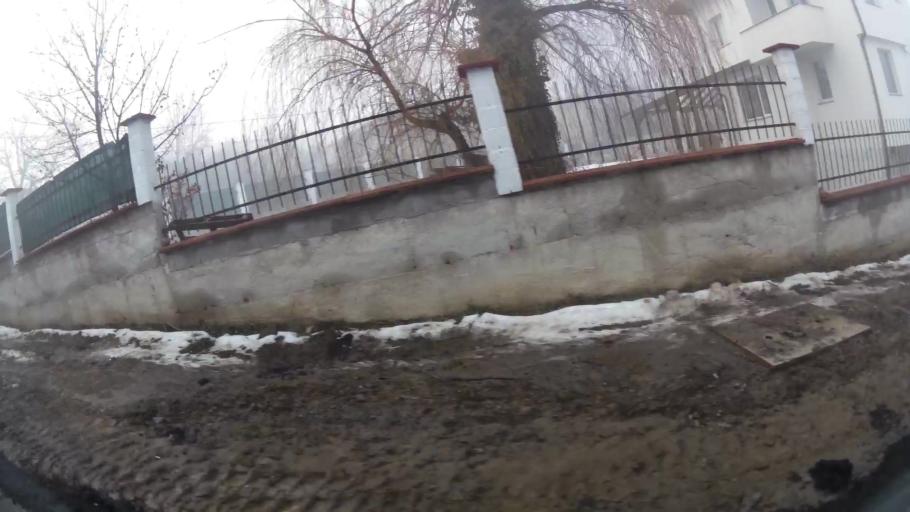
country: BG
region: Sofia-Capital
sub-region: Stolichna Obshtina
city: Sofia
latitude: 42.6554
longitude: 23.2552
